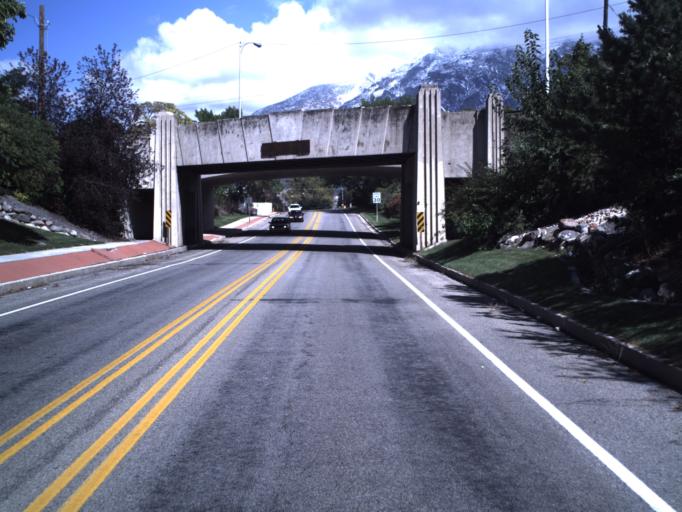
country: US
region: Utah
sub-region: Utah County
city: Springville
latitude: 40.1550
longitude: -111.6111
